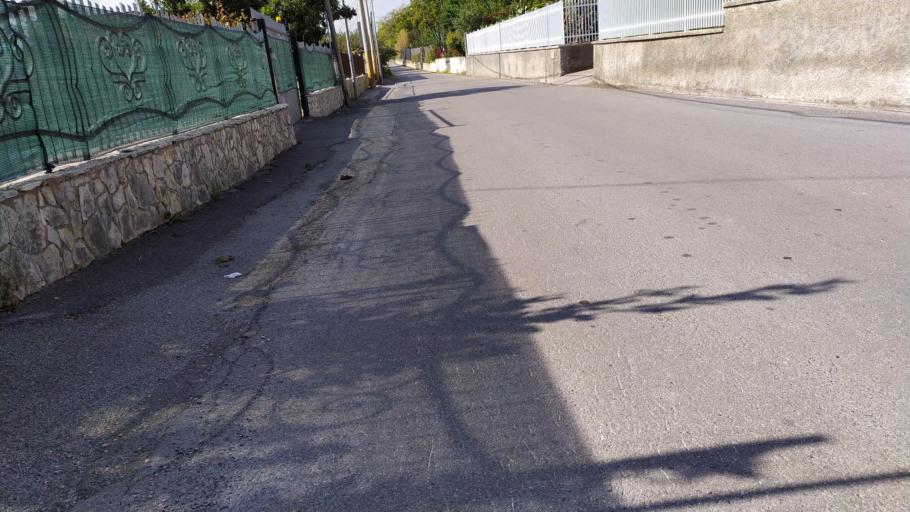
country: IT
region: Campania
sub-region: Provincia di Napoli
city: Striano
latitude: 40.8330
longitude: 14.5879
